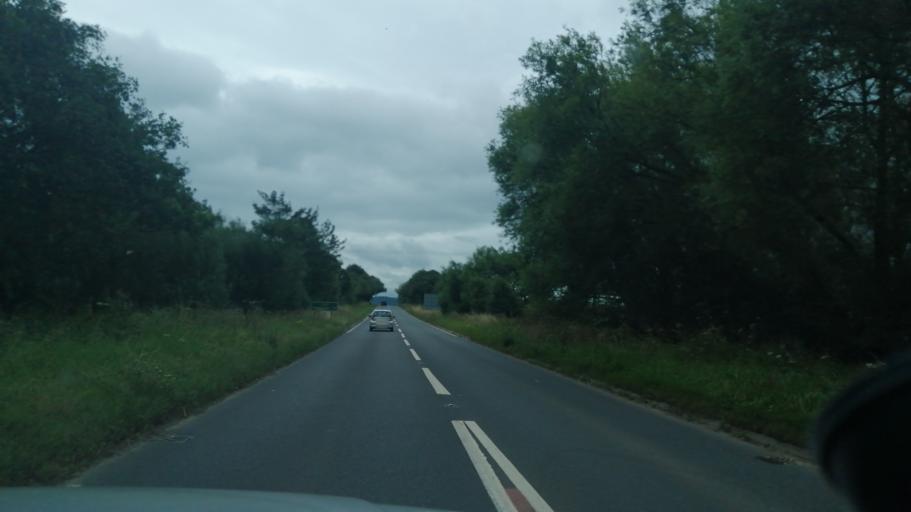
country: GB
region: England
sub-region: Herefordshire
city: Thruxton
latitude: 51.9980
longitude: -2.7923
